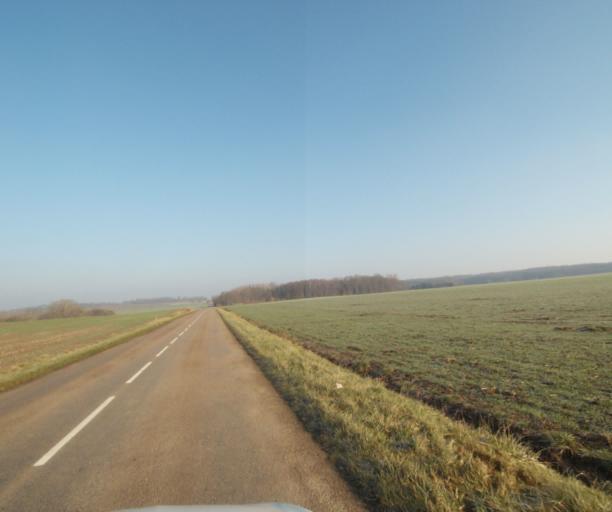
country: FR
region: Champagne-Ardenne
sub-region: Departement de la Haute-Marne
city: Montier-en-Der
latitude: 48.4164
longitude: 4.7424
